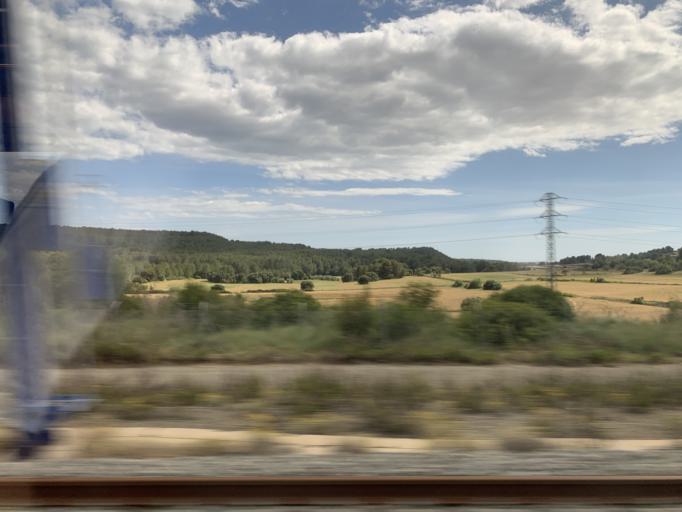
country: ES
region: Catalonia
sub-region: Provincia de Tarragona
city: La Secuita
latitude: 41.1932
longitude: 1.2653
